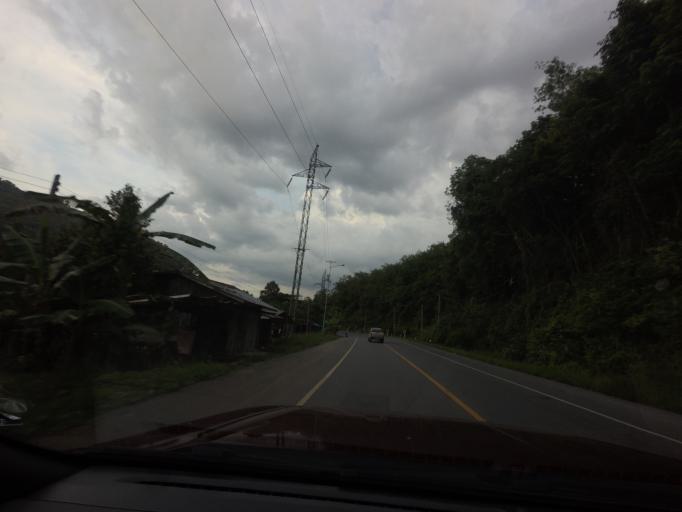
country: TH
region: Yala
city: Than To
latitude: 5.9993
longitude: 101.1921
